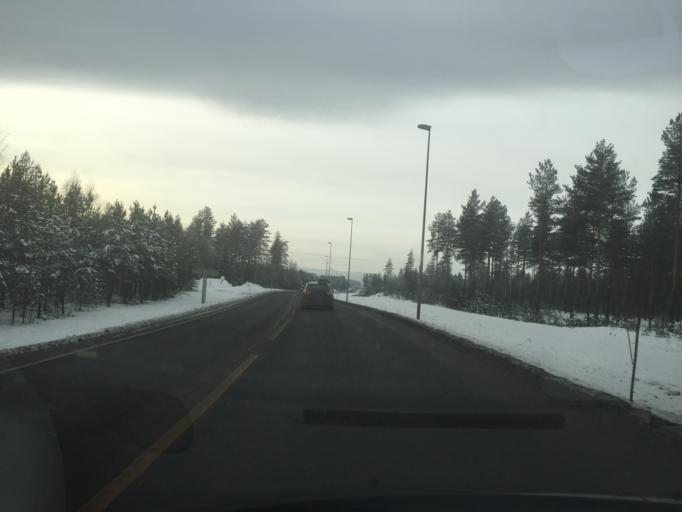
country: NO
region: Hedmark
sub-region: Elverum
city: Elverum
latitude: 60.9049
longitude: 11.6032
